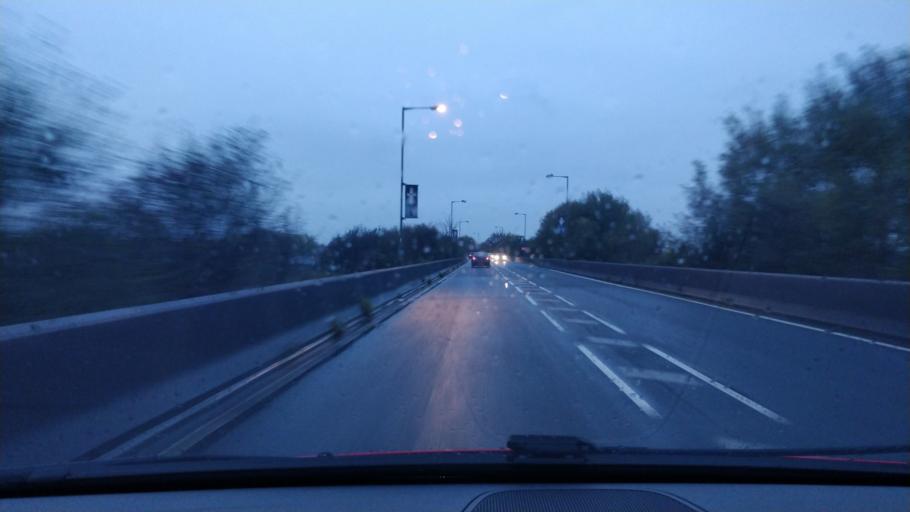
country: GB
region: England
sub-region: Lancashire
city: Great Marton
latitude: 53.7939
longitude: -3.0095
